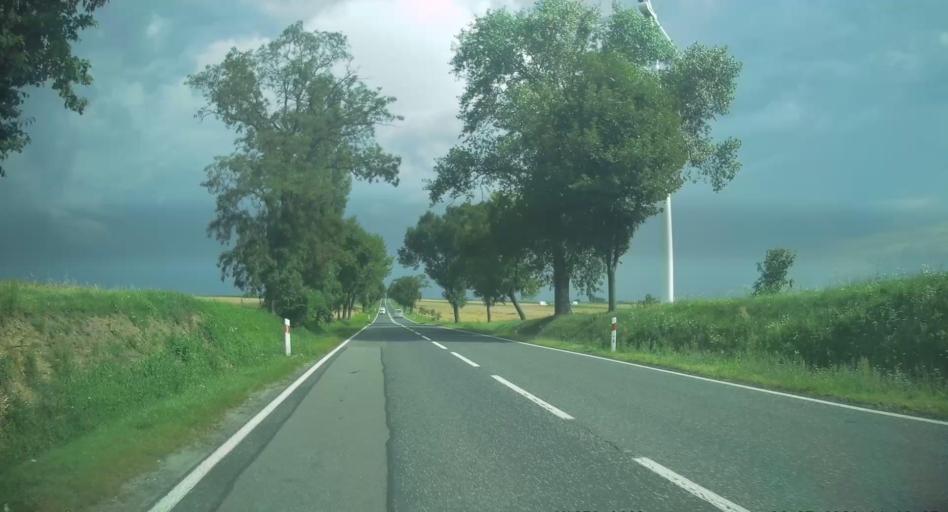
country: PL
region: Lodz Voivodeship
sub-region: Powiat skierniewicki
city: Gluchow
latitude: 51.7935
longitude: 20.0372
